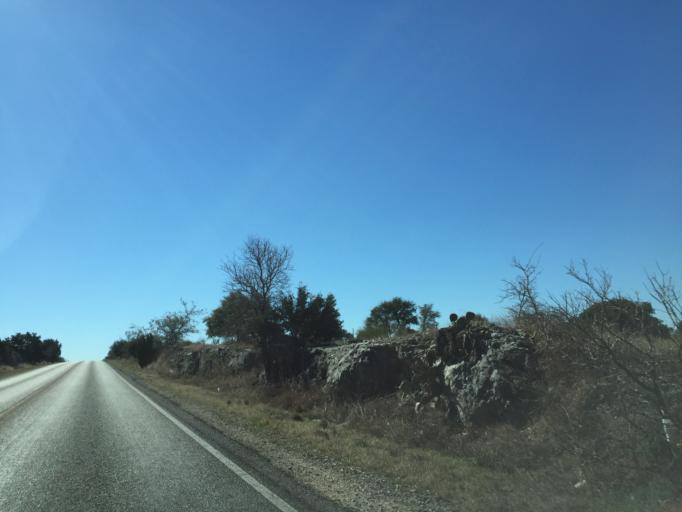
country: US
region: Texas
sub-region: Comal County
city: Garden Ridge
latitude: 29.7561
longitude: -98.3051
